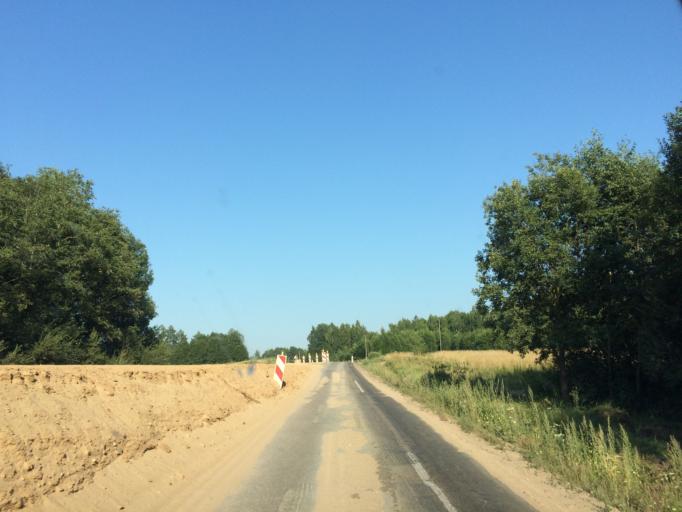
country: LV
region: Rezekne
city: Rezekne
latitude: 56.5101
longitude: 27.4442
